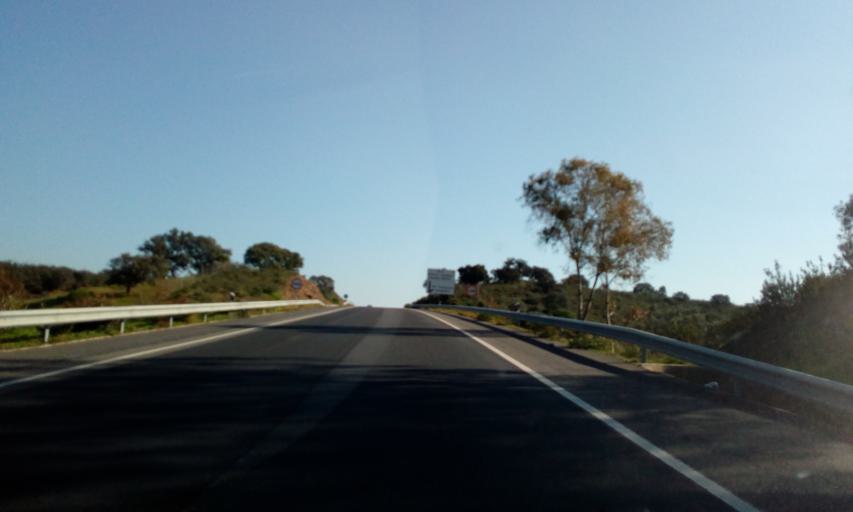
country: PT
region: Faro
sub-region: Castro Marim
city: Castro Marim
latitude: 37.2449
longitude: -7.4665
